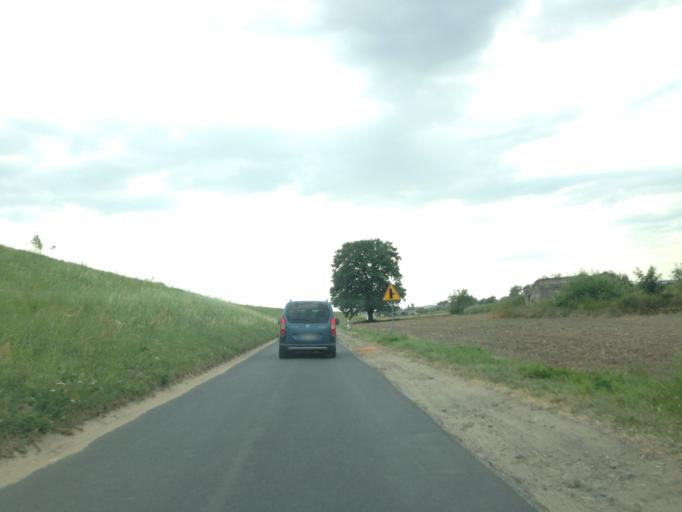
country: PL
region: Kujawsko-Pomorskie
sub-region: Powiat chelminski
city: Chelmno
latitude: 53.3674
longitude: 18.3965
